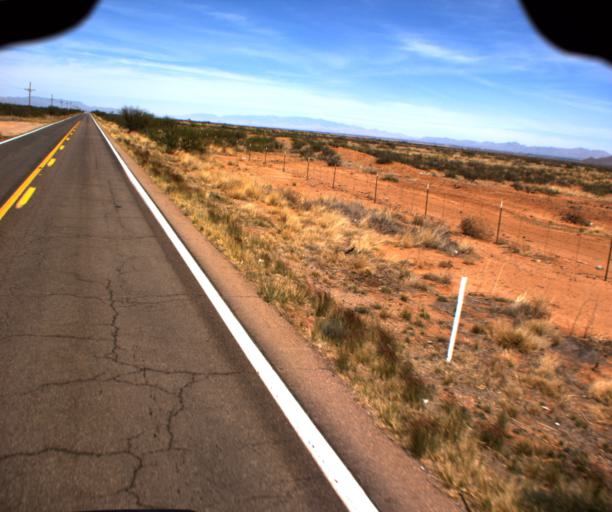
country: US
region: Arizona
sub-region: Cochise County
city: Tombstone
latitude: 31.9113
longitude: -109.8164
